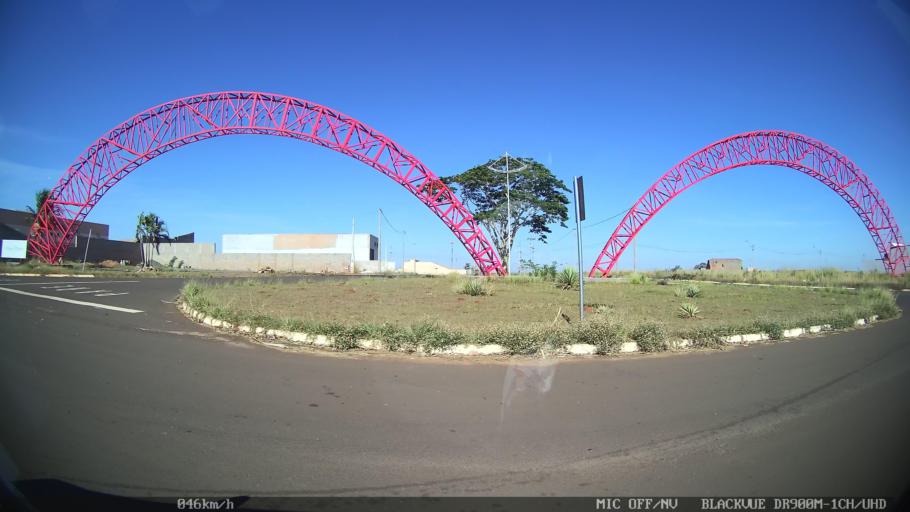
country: BR
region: Sao Paulo
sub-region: Olimpia
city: Olimpia
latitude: -20.7567
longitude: -48.9137
